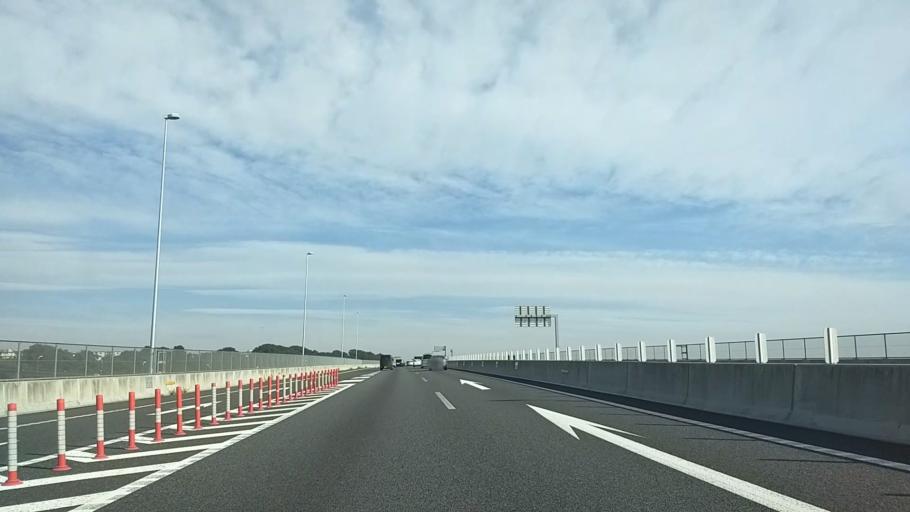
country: JP
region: Kanagawa
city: Zama
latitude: 35.4824
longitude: 139.3719
